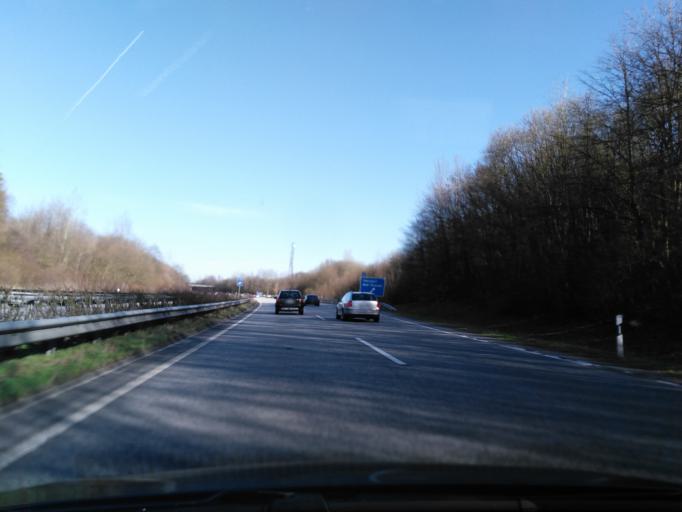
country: DE
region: Schleswig-Holstein
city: Melsdorf
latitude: 54.3068
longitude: 10.0264
